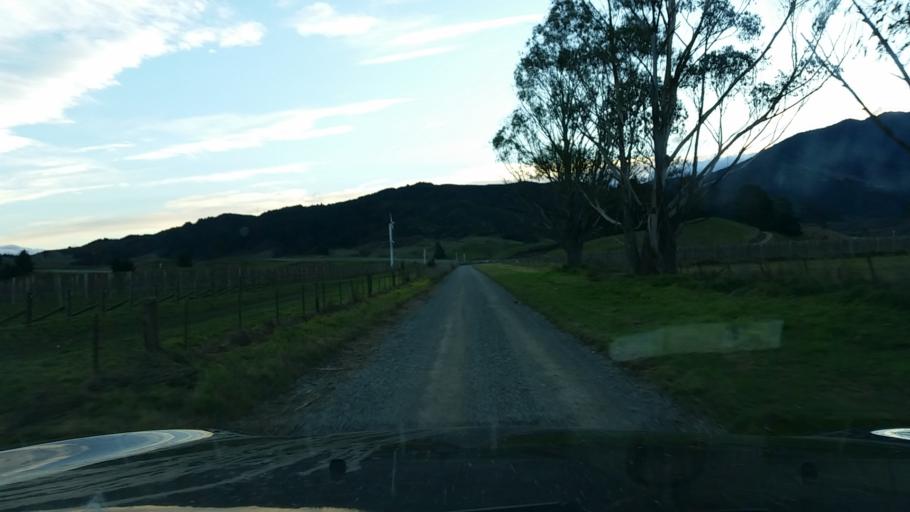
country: NZ
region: Marlborough
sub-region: Marlborough District
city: Blenheim
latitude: -41.5125
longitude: 173.5850
